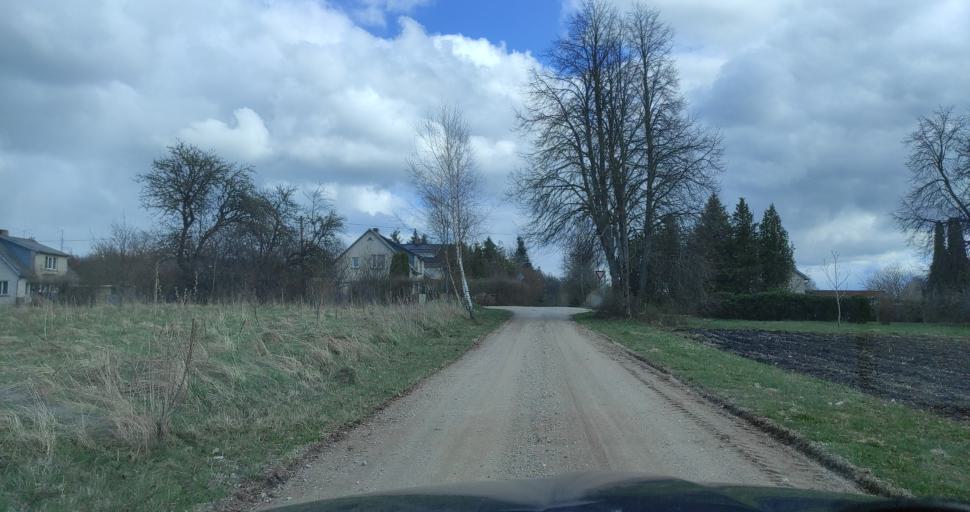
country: LV
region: Aizpute
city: Aizpute
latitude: 56.7153
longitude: 21.5892
